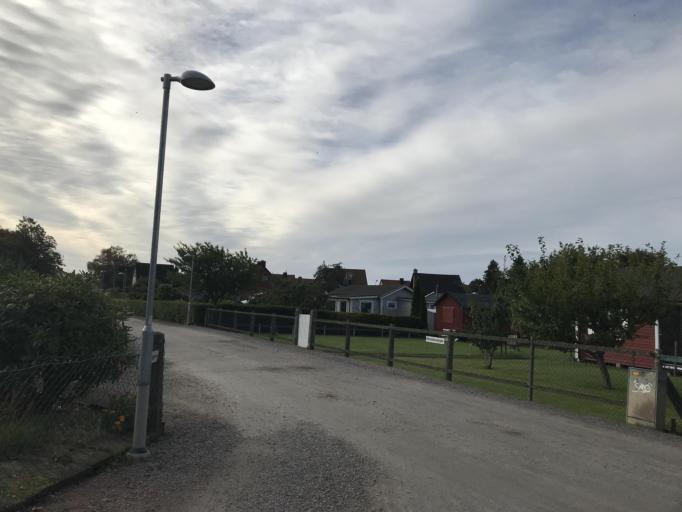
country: SE
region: Skane
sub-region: Landskrona
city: Landskrona
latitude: 55.8842
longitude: 12.8234
